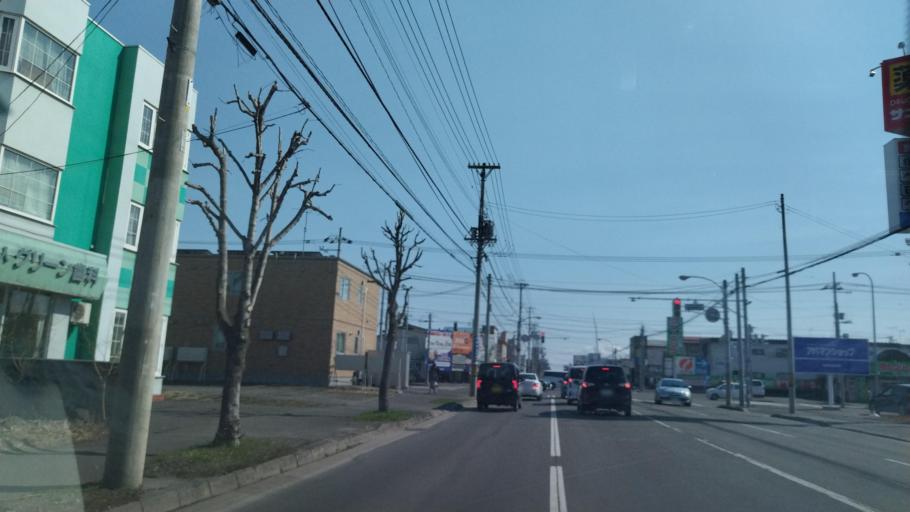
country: JP
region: Hokkaido
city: Obihiro
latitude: 42.8994
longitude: 143.2004
